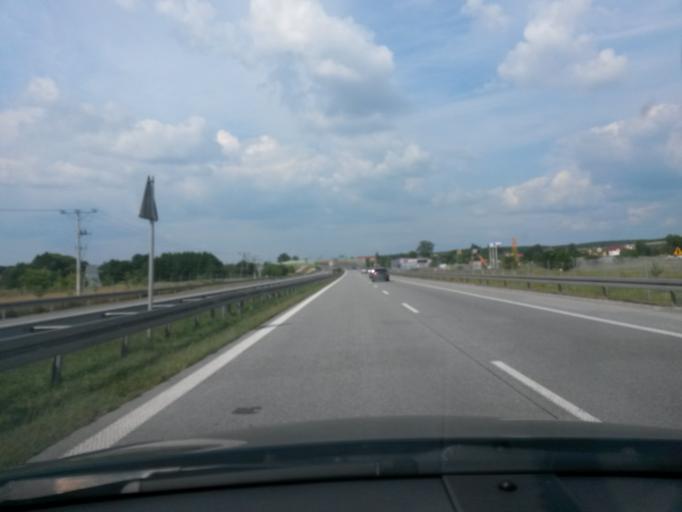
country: PL
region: Lodz Voivodeship
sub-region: Powiat rawski
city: Rawa Mazowiecka
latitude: 51.7625
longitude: 20.2660
